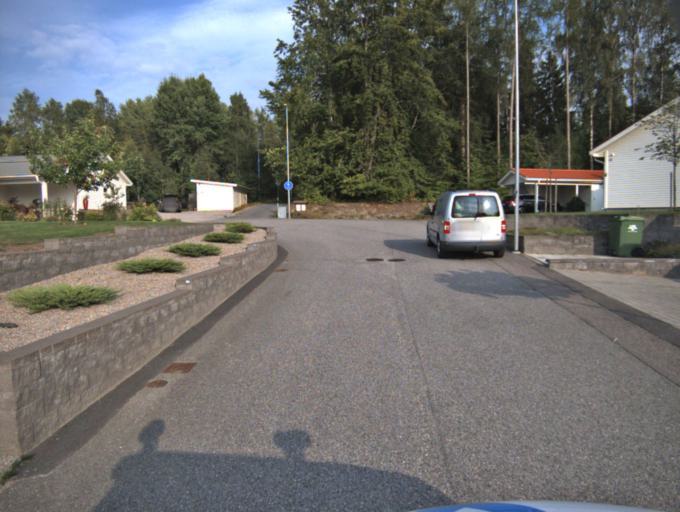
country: SE
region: Vaestra Goetaland
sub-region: Ulricehamns Kommun
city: Ulricehamn
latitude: 57.7834
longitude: 13.4317
